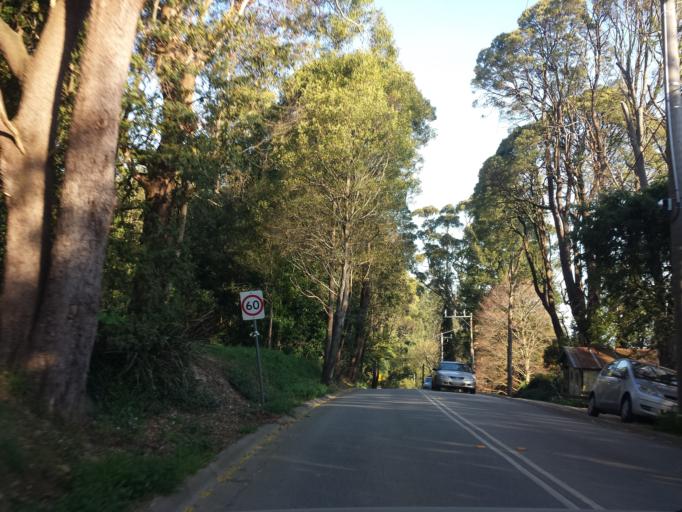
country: AU
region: Victoria
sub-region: Yarra Ranges
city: Ferny Creek
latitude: -37.8849
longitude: 145.3435
